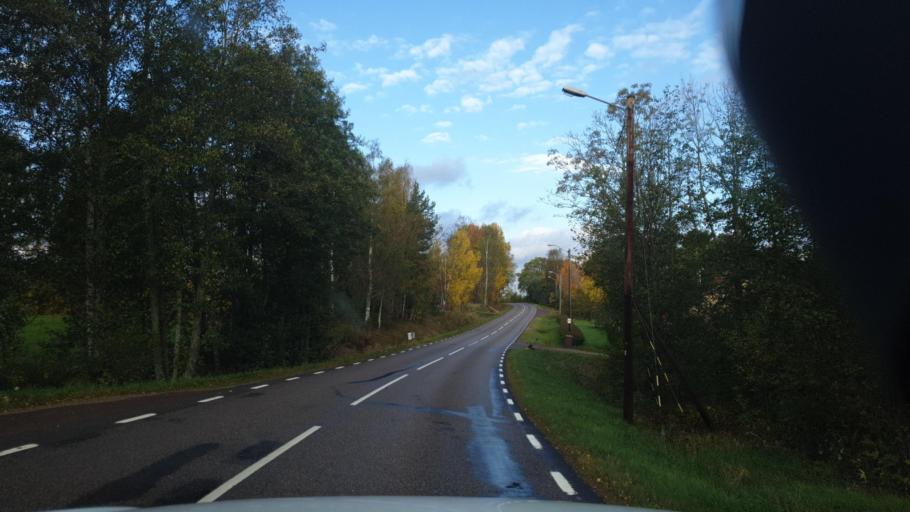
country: SE
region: Vaermland
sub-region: Arvika Kommun
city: Arvika
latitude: 59.4789
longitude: 12.7114
